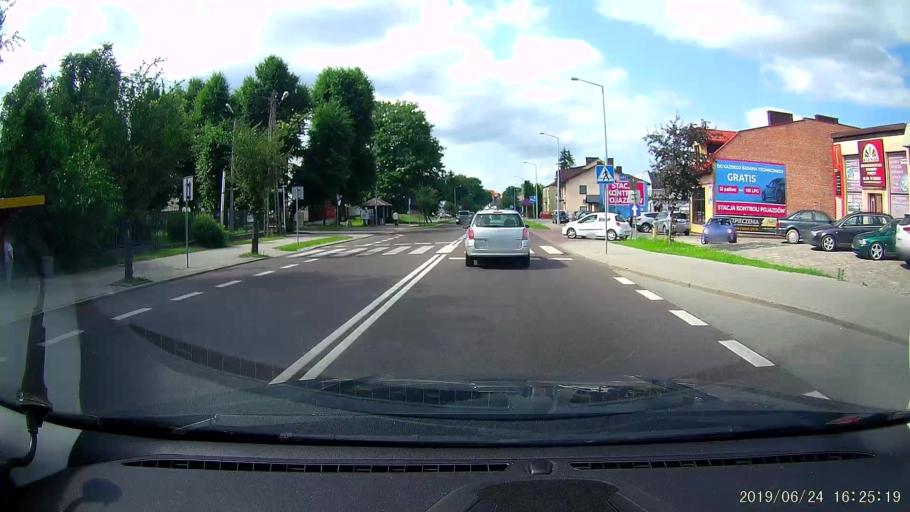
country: PL
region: Lublin Voivodeship
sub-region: Powiat tomaszowski
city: Tomaszow Lubelski
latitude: 50.4431
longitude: 23.4176
